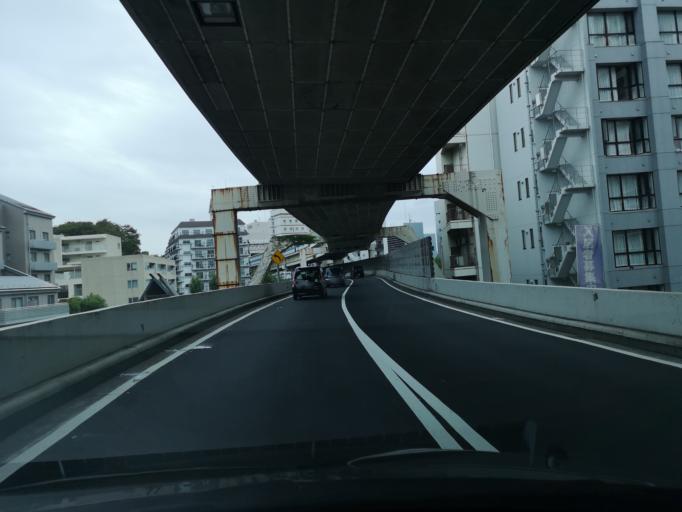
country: JP
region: Tokyo
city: Tokyo
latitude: 35.6538
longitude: 139.7374
